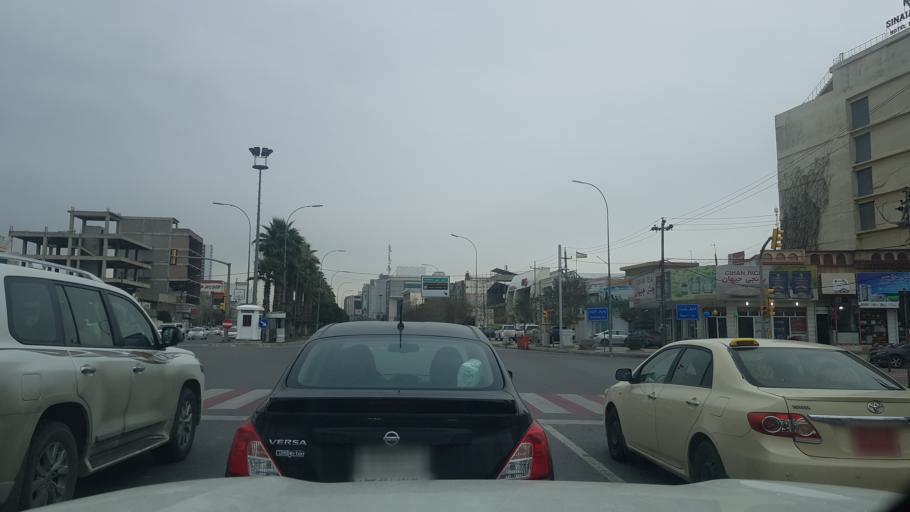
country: IQ
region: Arbil
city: Erbil
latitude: 36.1767
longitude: 43.9992
